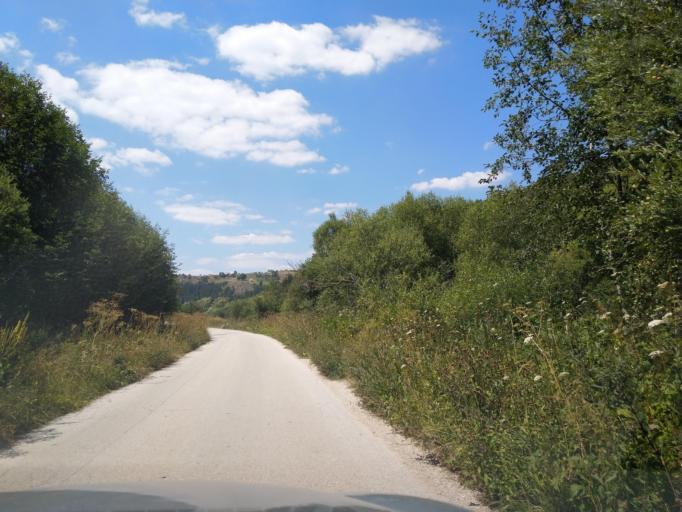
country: RS
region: Central Serbia
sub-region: Zlatiborski Okrug
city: Nova Varos
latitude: 43.4806
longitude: 19.9776
